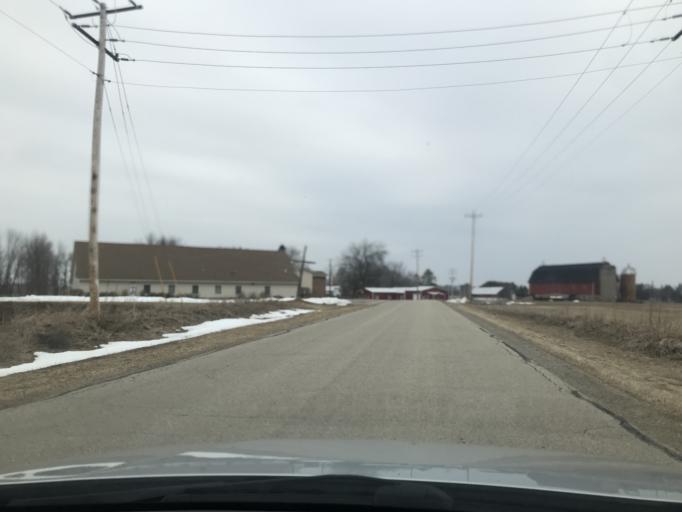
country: US
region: Wisconsin
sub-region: Marinette County
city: Peshtigo
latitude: 45.0466
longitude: -87.8524
